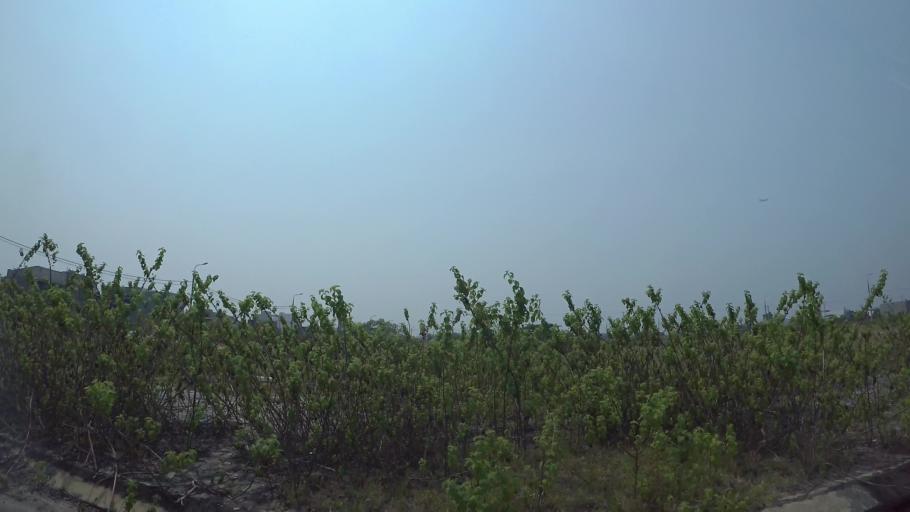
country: VN
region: Da Nang
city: Cam Le
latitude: 15.9815
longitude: 108.2179
